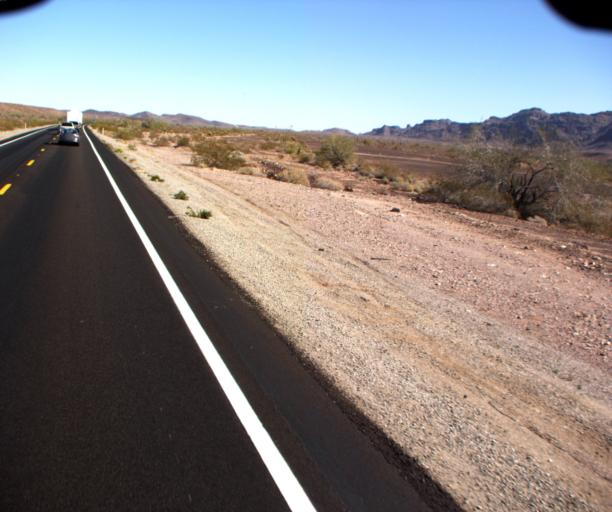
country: US
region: Arizona
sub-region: La Paz County
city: Quartzsite
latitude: 33.1810
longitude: -114.2755
